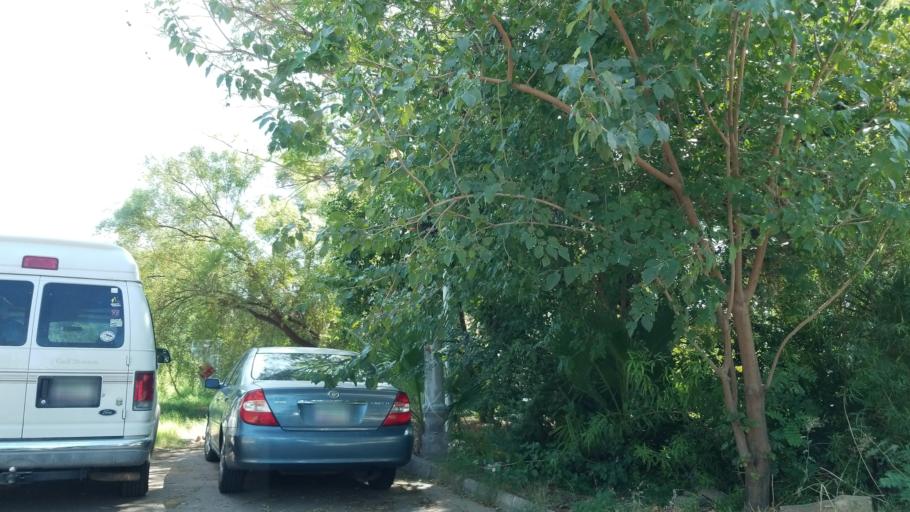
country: US
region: Arizona
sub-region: Maricopa County
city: Glendale
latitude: 33.5575
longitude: -112.0959
